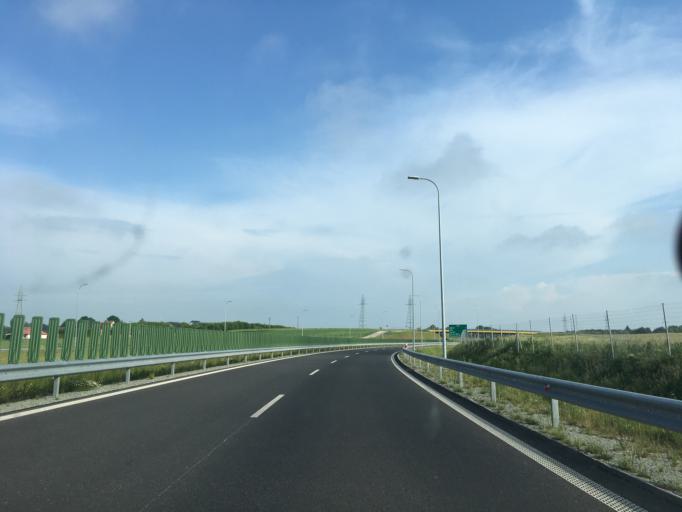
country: PL
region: West Pomeranian Voivodeship
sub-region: Koszalin
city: Koszalin
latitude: 54.1861
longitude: 16.1235
